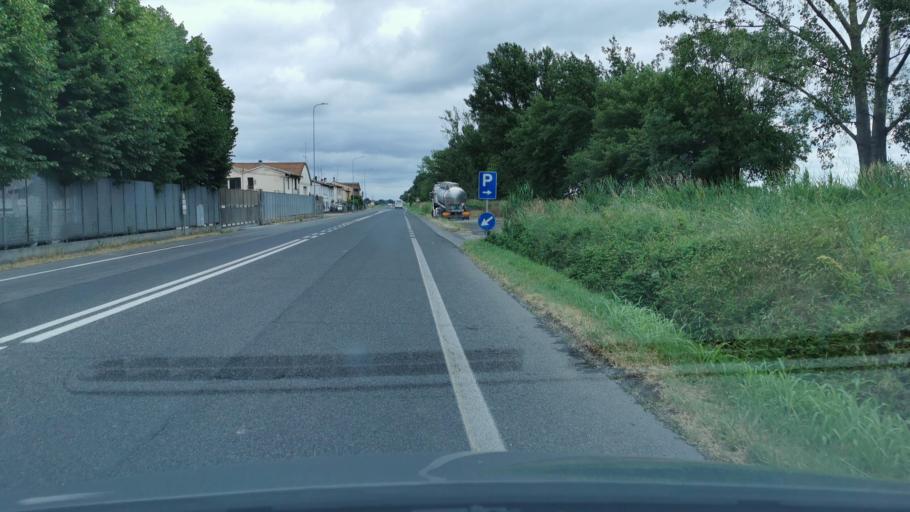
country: IT
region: Emilia-Romagna
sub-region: Provincia di Ravenna
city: Granarolo
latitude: 44.3306
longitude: 11.9121
